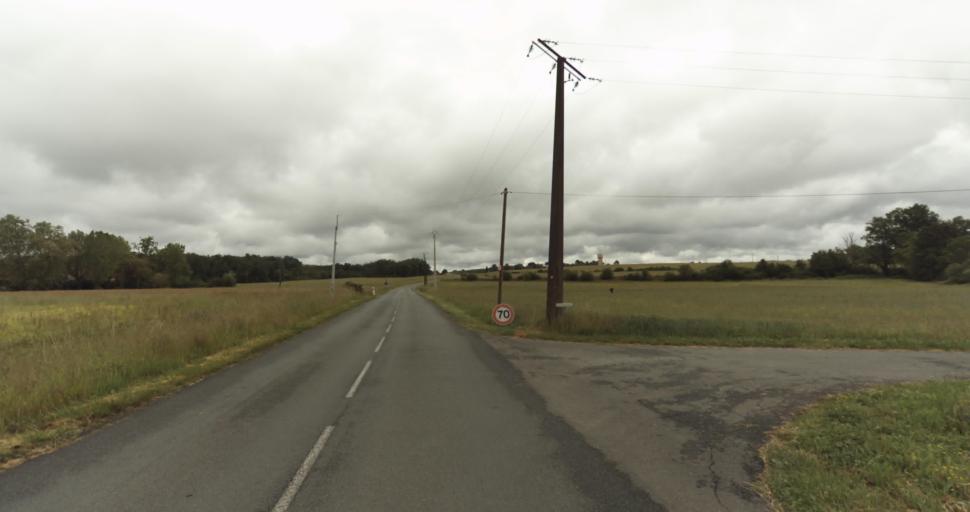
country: FR
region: Aquitaine
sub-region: Departement de la Dordogne
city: Belves
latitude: 44.7021
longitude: 0.9201
